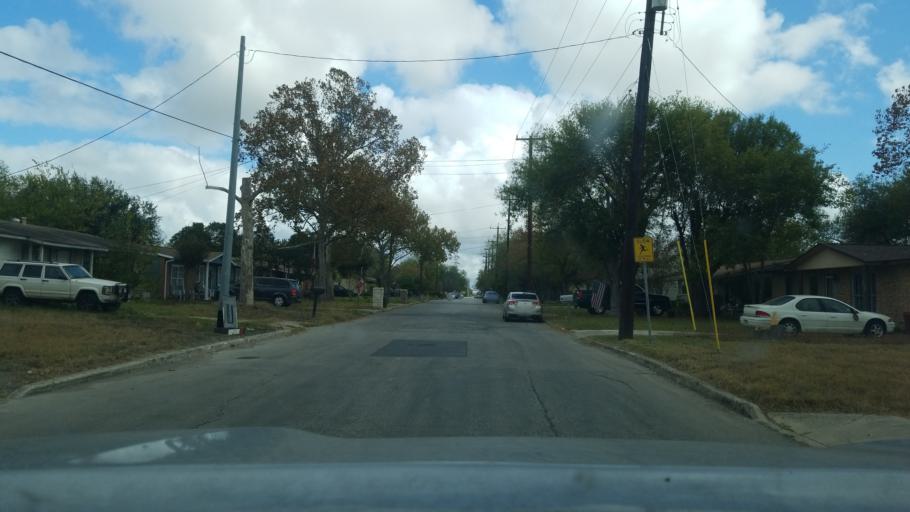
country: US
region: Texas
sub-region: Bexar County
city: Universal City
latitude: 29.5420
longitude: -98.2944
